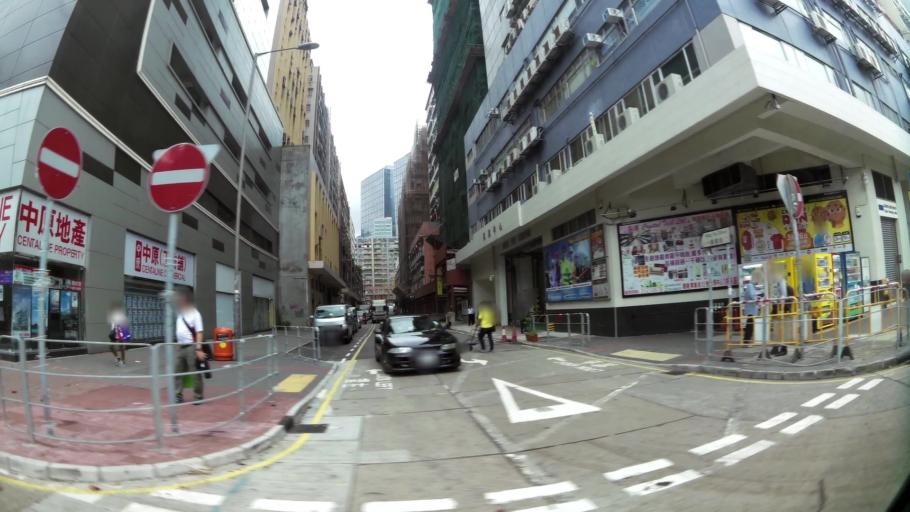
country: HK
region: Kowloon City
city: Kowloon
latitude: 22.3080
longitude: 114.2270
